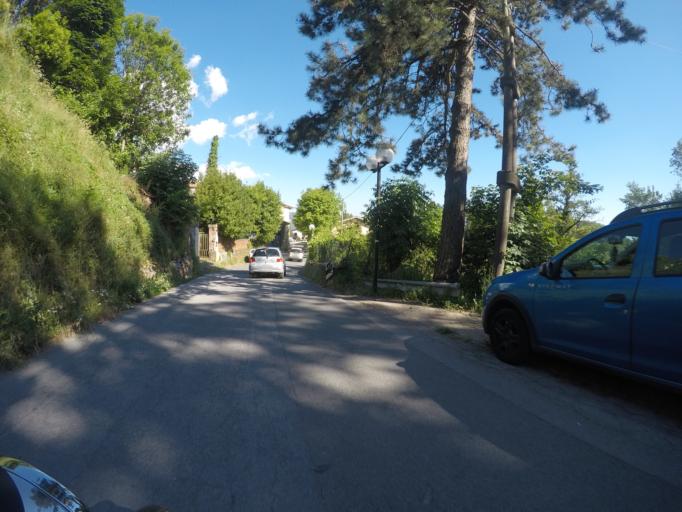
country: IT
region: Liguria
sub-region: Provincia di La Spezia
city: Casano-Dogana-Isola
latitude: 44.1138
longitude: 10.0728
